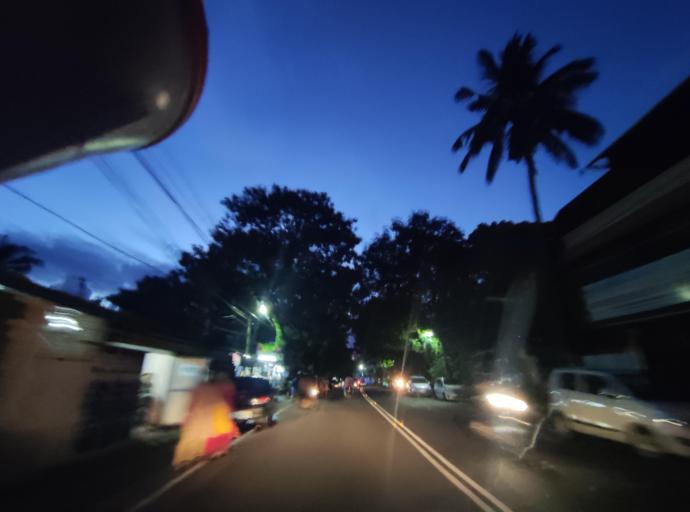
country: IN
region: Kerala
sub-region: Thiruvananthapuram
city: Thiruvananthapuram
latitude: 8.5391
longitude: 76.9636
